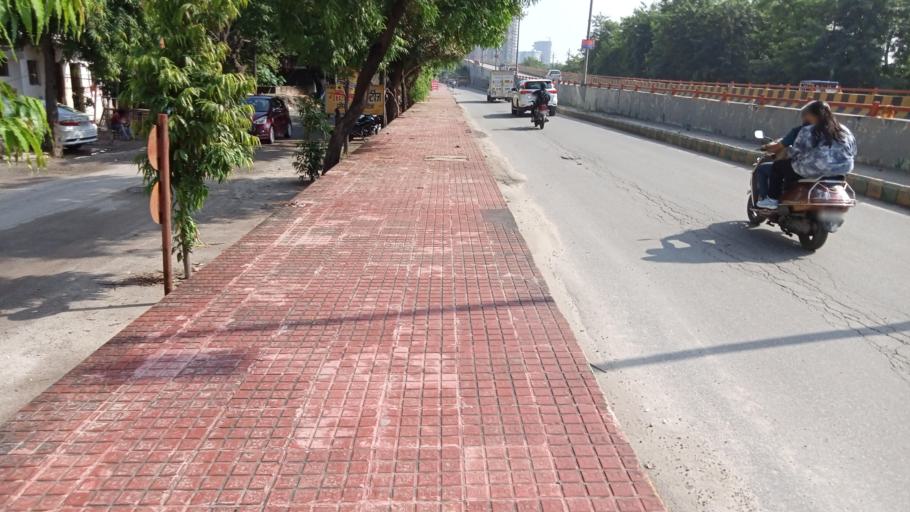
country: IN
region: Uttar Pradesh
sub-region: Ghaziabad
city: Ghaziabad
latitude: 28.6614
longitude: 77.3741
